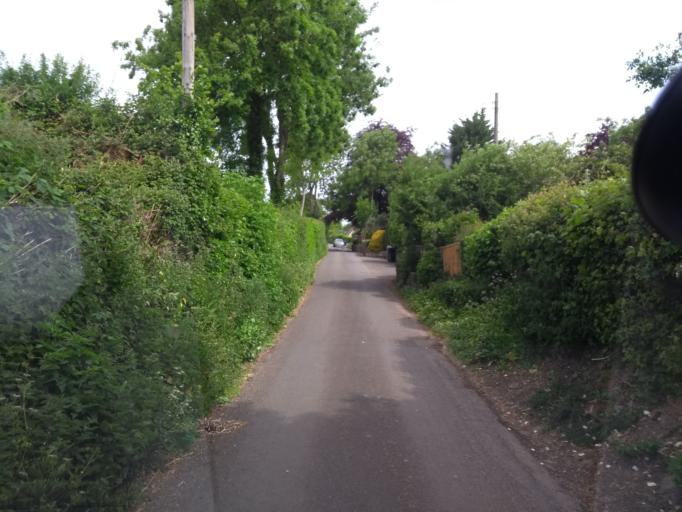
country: GB
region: England
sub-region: Somerset
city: Williton
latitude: 51.1820
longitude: -3.2179
